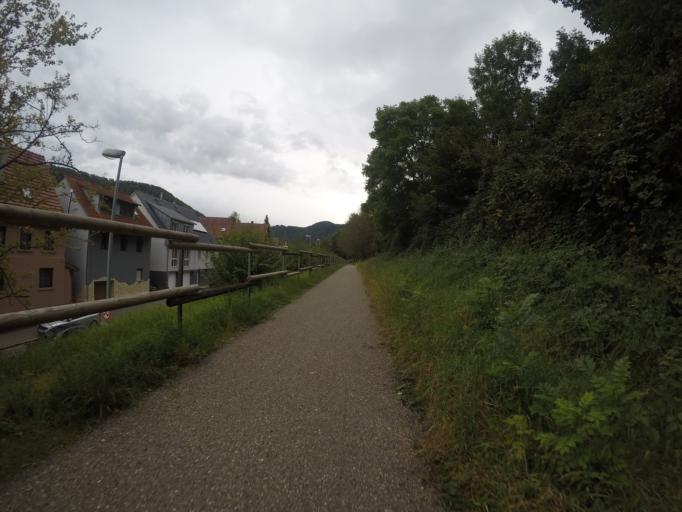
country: DE
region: Baden-Wuerttemberg
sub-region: Tuebingen Region
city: Pfullingen
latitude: 48.4327
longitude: 9.2549
